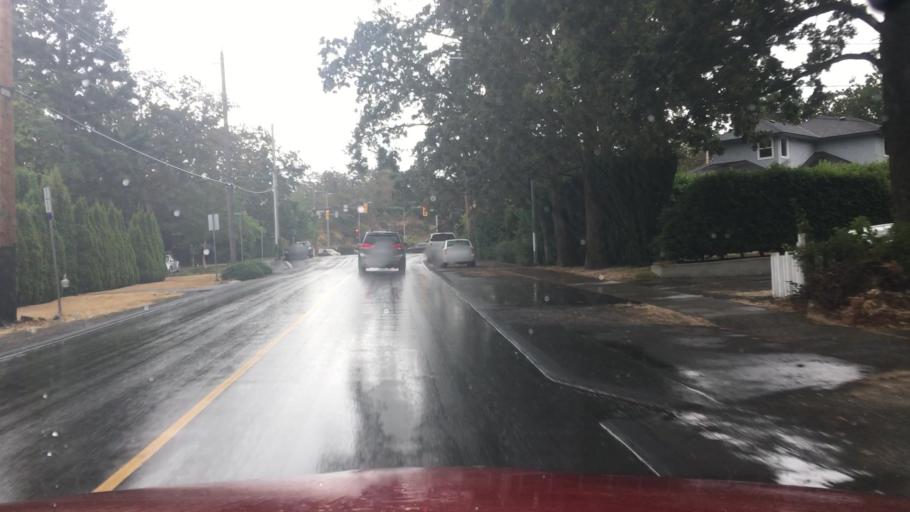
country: CA
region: British Columbia
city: Victoria
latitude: 48.4681
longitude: -123.3501
